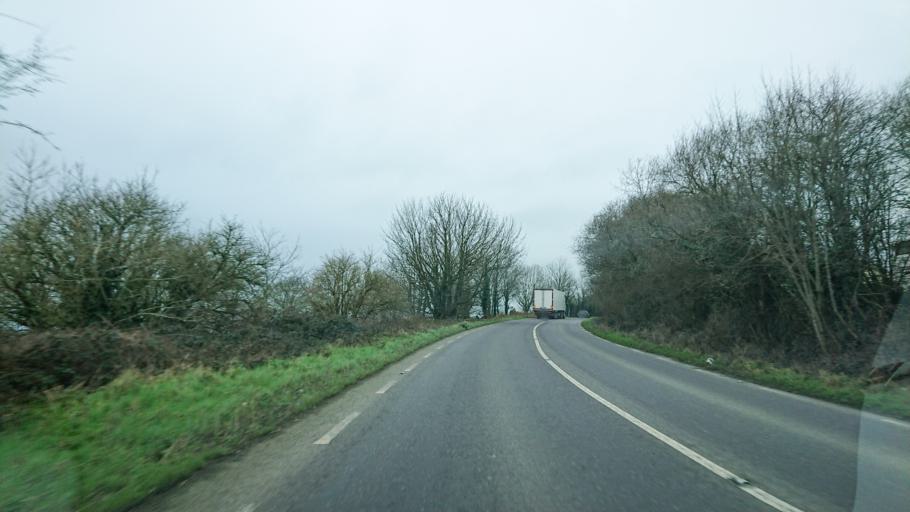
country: IE
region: Munster
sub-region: County Cork
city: Bandon
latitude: 51.7426
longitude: -8.8135
